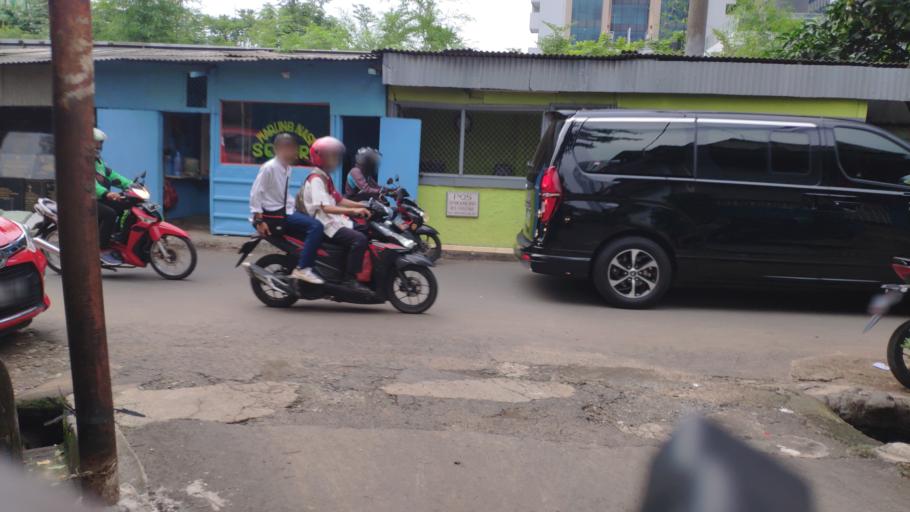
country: ID
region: Jakarta Raya
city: Jakarta
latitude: -6.2219
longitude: 106.8410
